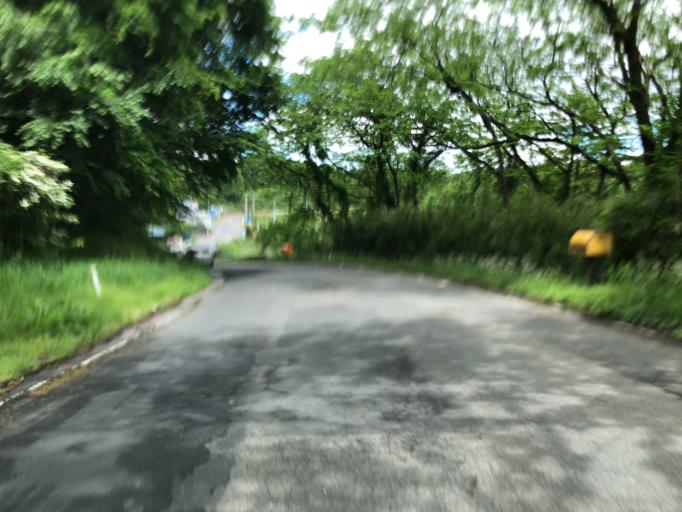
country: JP
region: Fukushima
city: Motomiya
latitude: 37.4769
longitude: 140.4449
